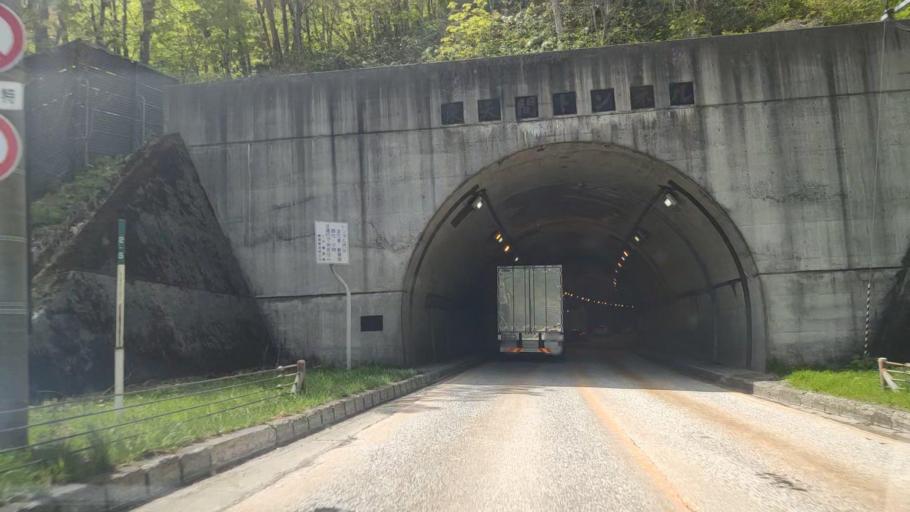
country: JP
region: Aomori
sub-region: Misawa Shi
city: Inuotose
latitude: 40.7820
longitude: 141.0612
